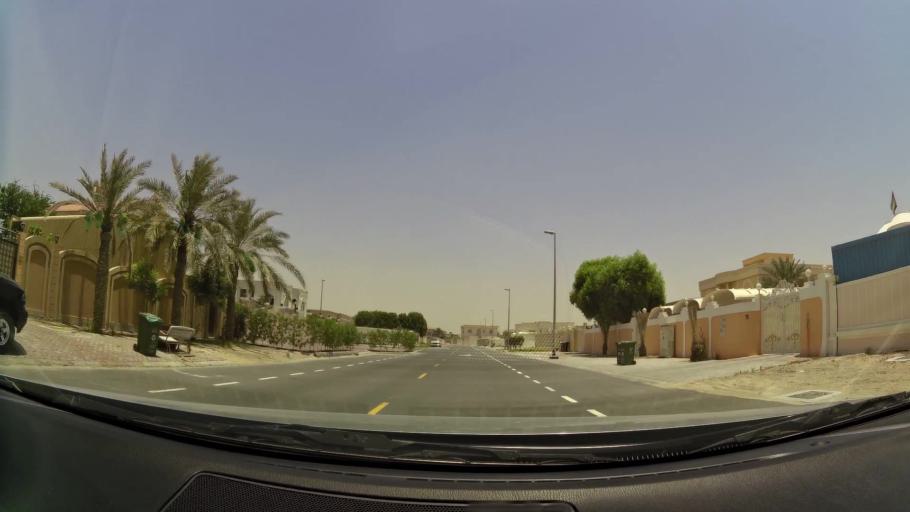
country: AE
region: Dubai
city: Dubai
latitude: 25.0985
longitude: 55.1911
